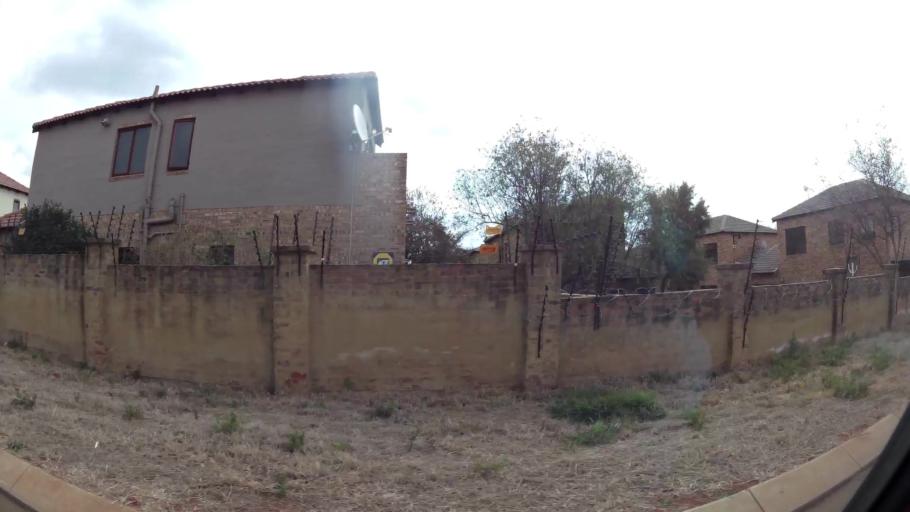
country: ZA
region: Gauteng
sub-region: City of Johannesburg Metropolitan Municipality
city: Roodepoort
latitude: -26.1000
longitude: 27.8808
